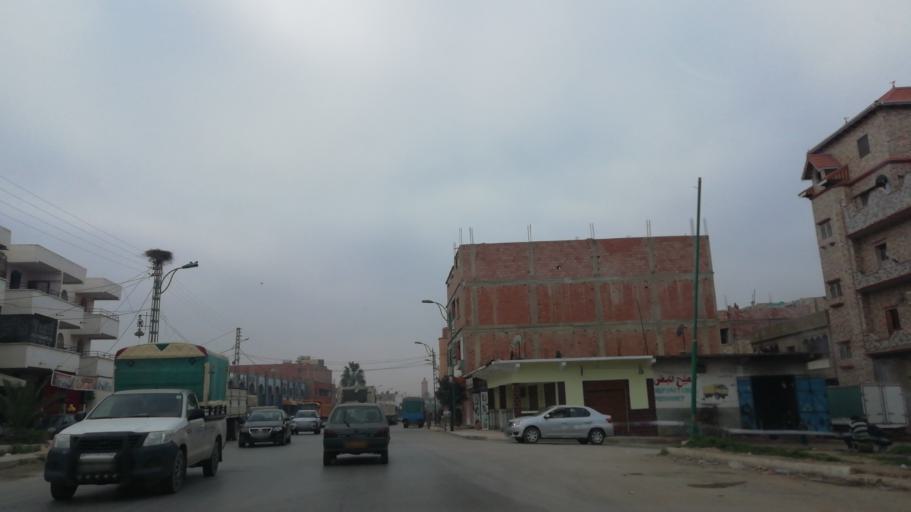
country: DZ
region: Relizane
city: Djidiouia
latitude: 35.9094
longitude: 0.7794
